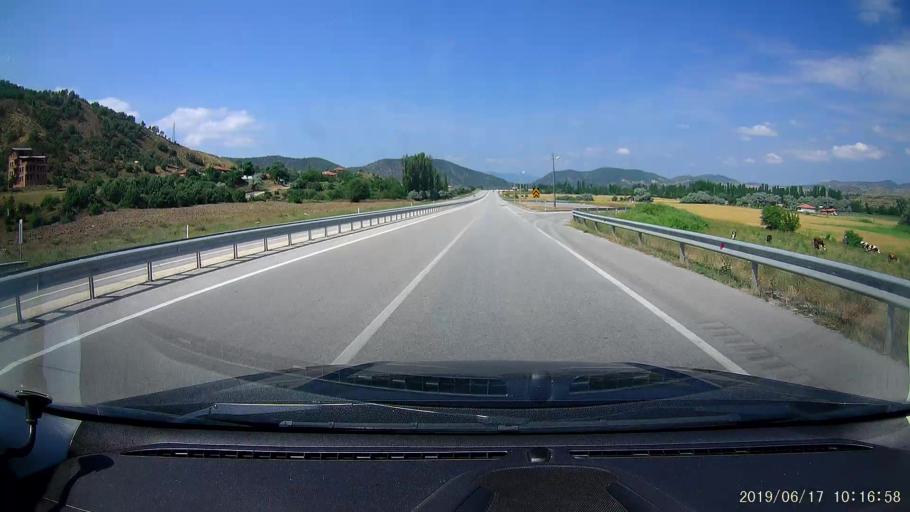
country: TR
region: Corum
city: Osmancik
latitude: 40.9849
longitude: 34.9619
